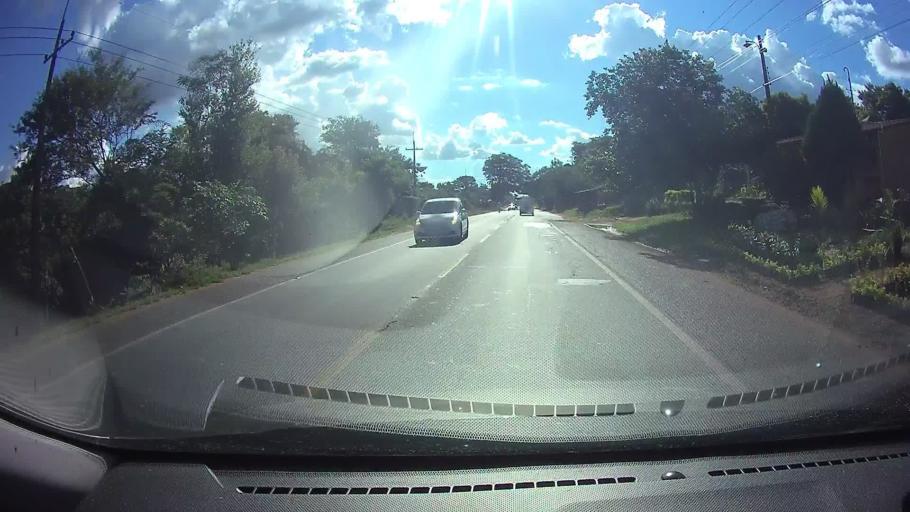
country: PY
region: Cordillera
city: Caacupe
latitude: -25.3883
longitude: -57.1044
